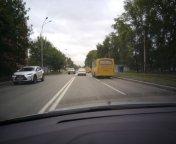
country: RU
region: Sverdlovsk
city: Sovkhoznyy
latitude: 56.7770
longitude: 60.6118
